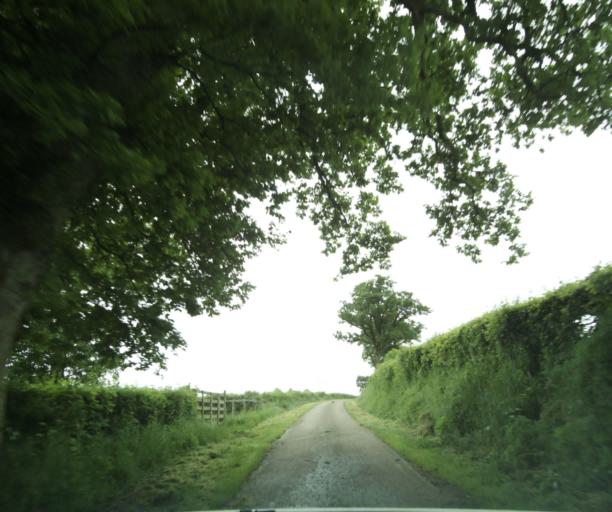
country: FR
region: Bourgogne
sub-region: Departement de Saone-et-Loire
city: Charolles
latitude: 46.4615
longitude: 4.2896
